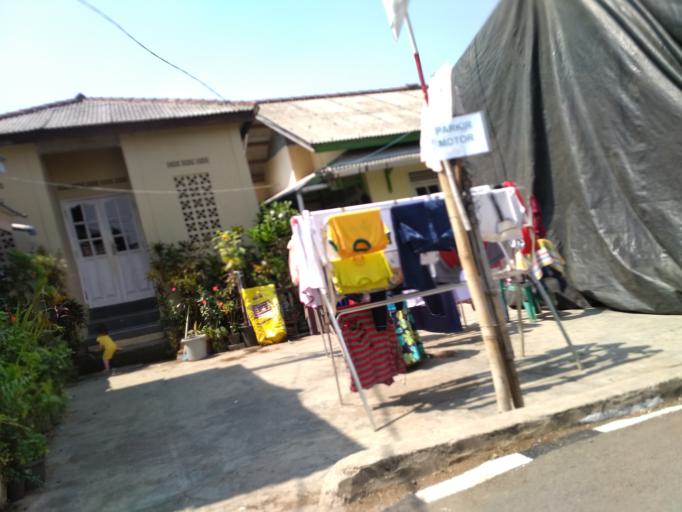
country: ID
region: West Java
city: Ciampea
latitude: -6.5637
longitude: 106.7483
